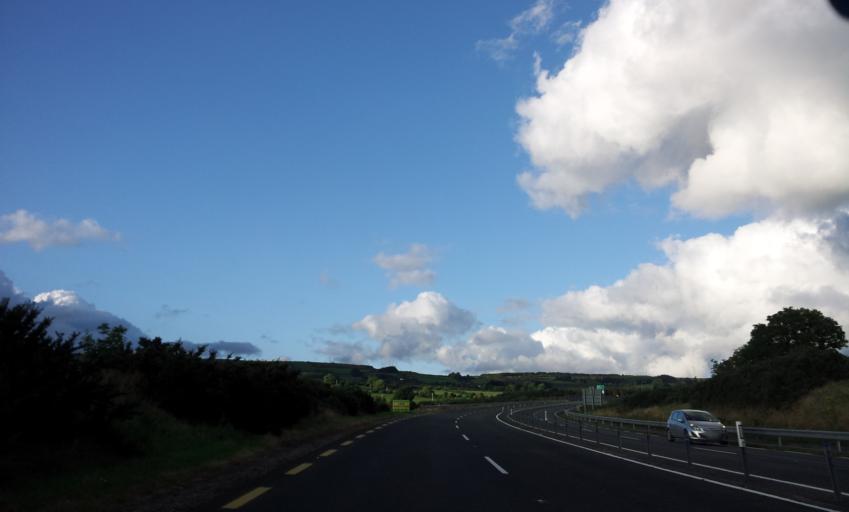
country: IE
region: Munster
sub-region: Ciarrai
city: Castleisland
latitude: 52.2571
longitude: -9.4711
